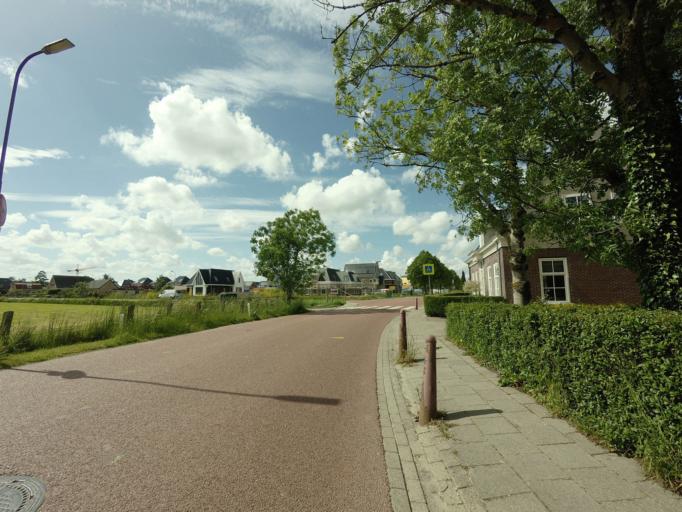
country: NL
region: North Holland
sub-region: Gemeente Hoorn
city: Hoorn
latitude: 52.6709
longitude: 5.0992
